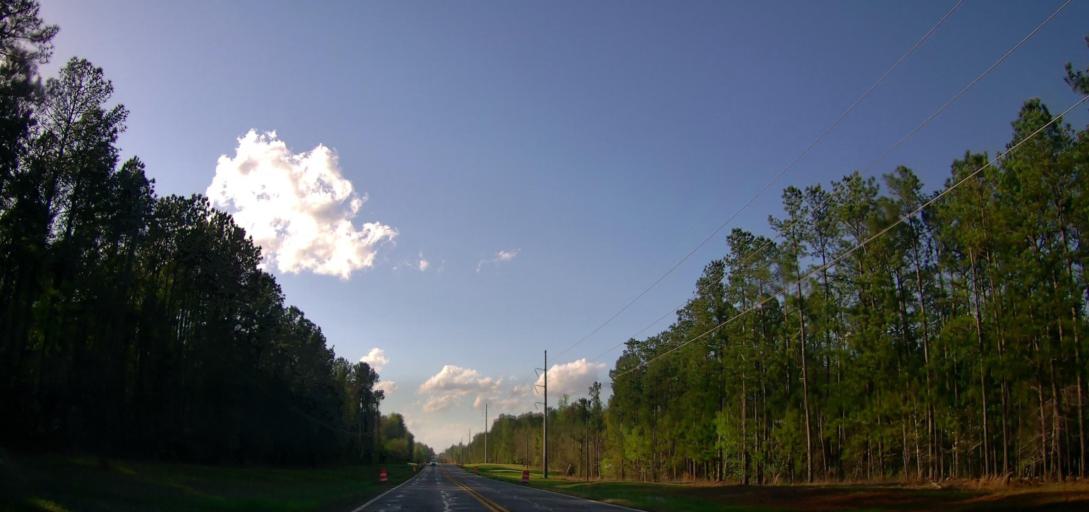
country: US
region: Georgia
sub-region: Baldwin County
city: Milledgeville
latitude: 33.1295
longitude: -83.3183
